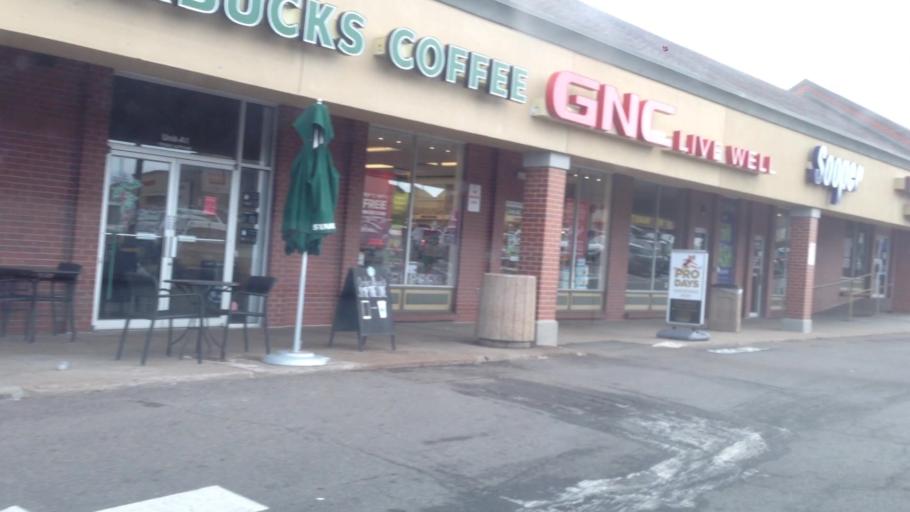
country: US
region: Colorado
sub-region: Adams County
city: Aurora
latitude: 39.6728
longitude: -104.7886
